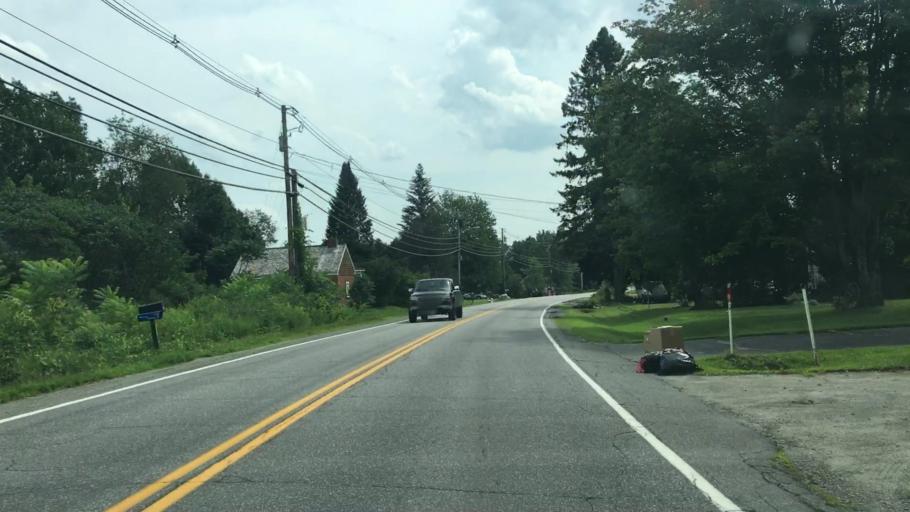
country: US
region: Maine
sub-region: Kennebec County
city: Winslow
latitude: 44.5093
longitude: -69.6308
